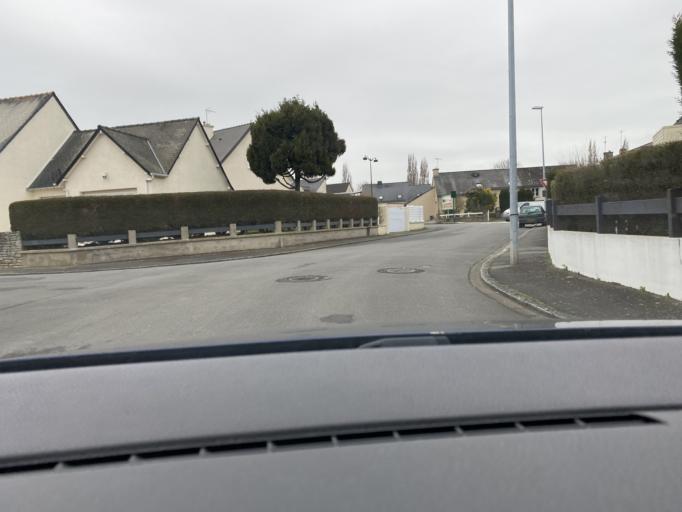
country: FR
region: Brittany
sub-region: Departement d'Ille-et-Vilaine
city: Melesse
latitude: 48.2220
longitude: -1.6909
